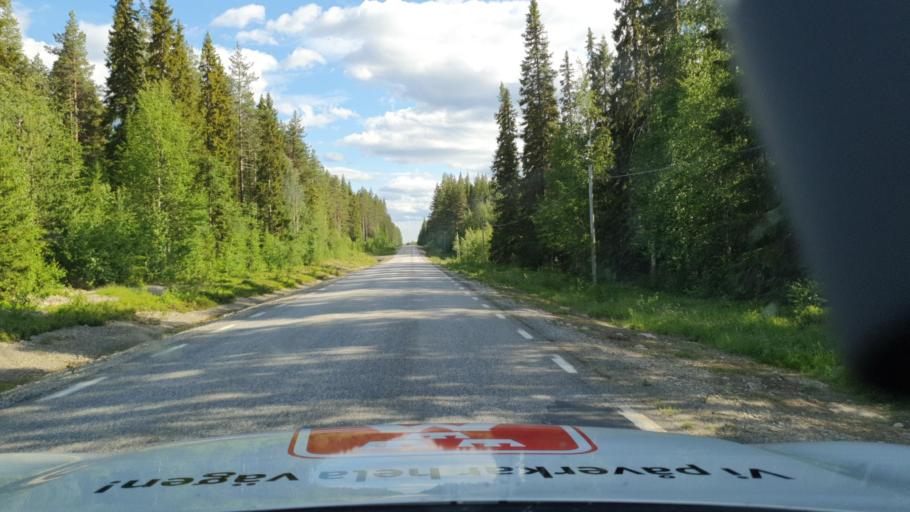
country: SE
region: Vaesterbotten
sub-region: Skelleftea Kommun
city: Langsele
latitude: 64.7397
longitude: 19.9523
